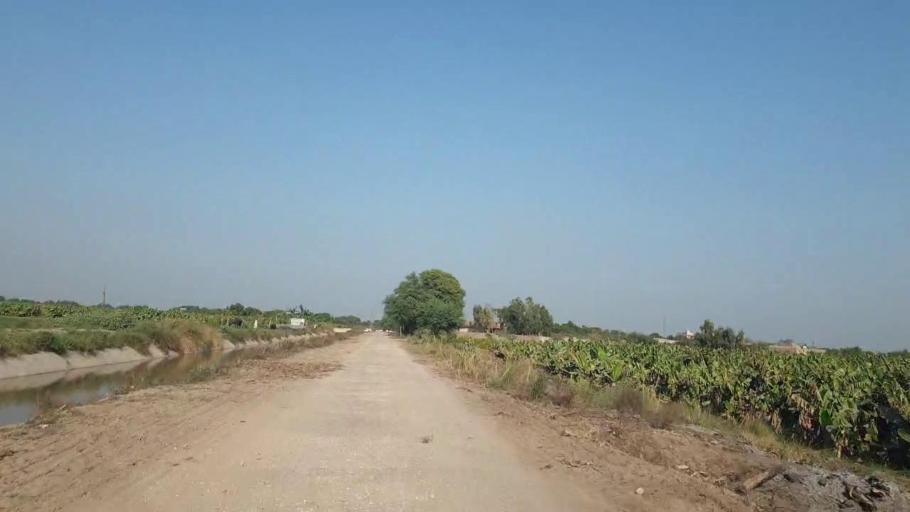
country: PK
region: Sindh
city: Matiari
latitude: 25.5381
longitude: 68.4416
